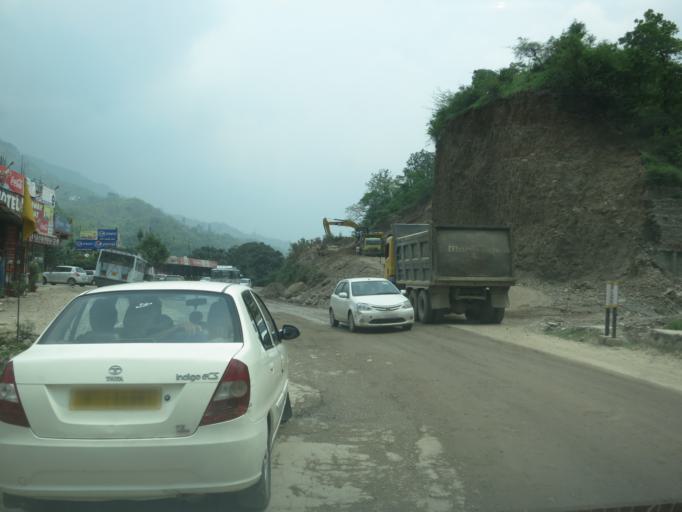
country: IN
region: Himachal Pradesh
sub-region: Mandi
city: Sundarnagar
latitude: 31.4528
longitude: 76.8582
